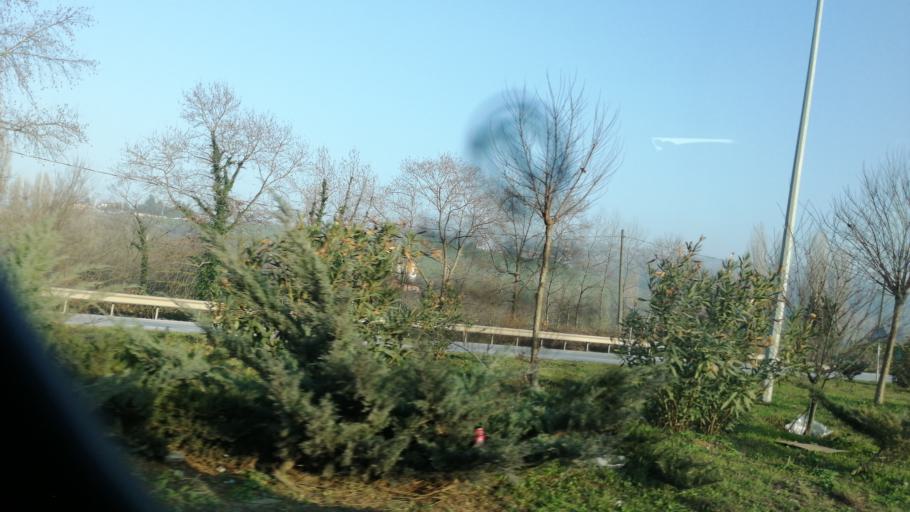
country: TR
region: Yalova
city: Yalova
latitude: 40.6213
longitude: 29.2710
